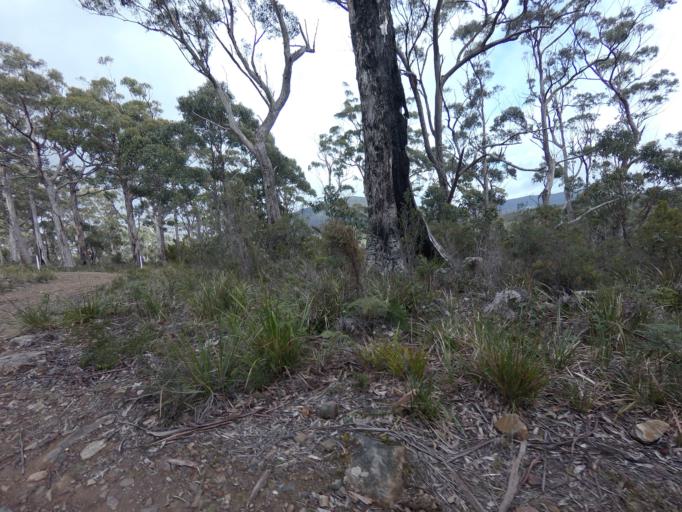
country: AU
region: Tasmania
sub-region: Huon Valley
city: Geeveston
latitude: -43.4602
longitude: 146.9095
